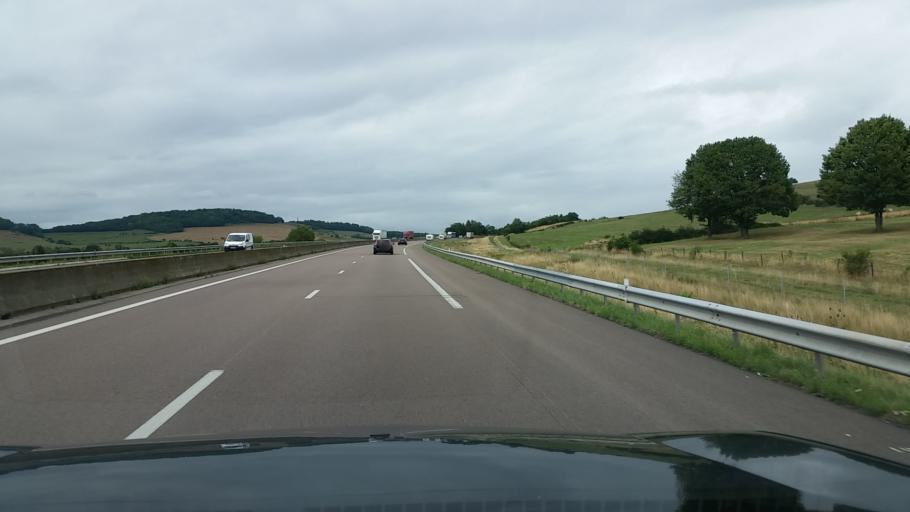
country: FR
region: Lorraine
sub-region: Departement des Vosges
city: Chatenois
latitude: 48.3617
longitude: 5.8668
